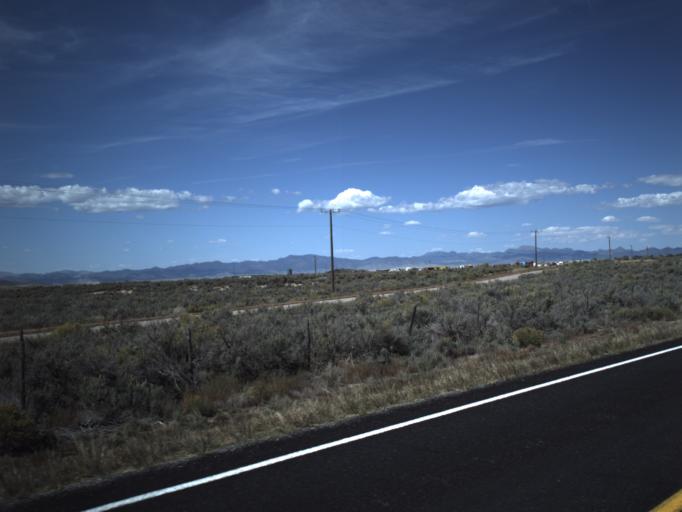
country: US
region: Utah
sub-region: Washington County
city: Enterprise
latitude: 37.6706
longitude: -113.6609
